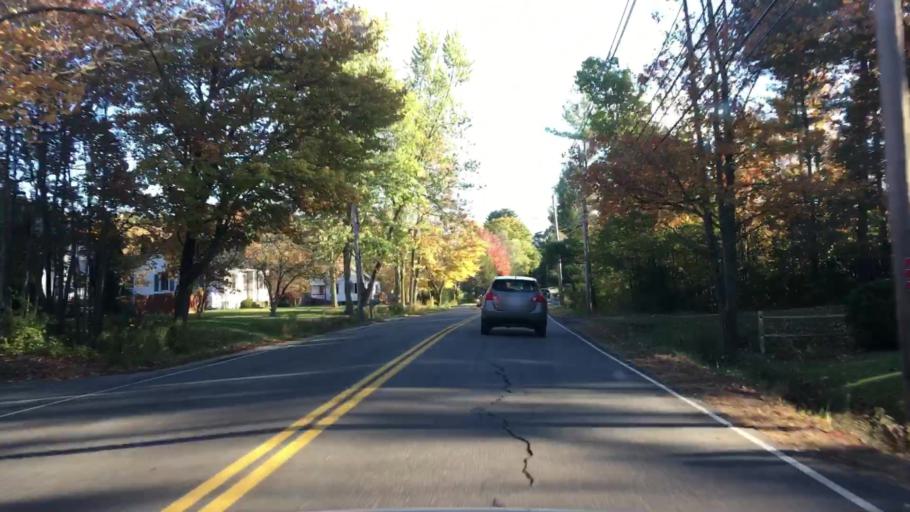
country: US
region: Maine
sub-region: Cumberland County
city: Scarborough
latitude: 43.6085
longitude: -70.3393
